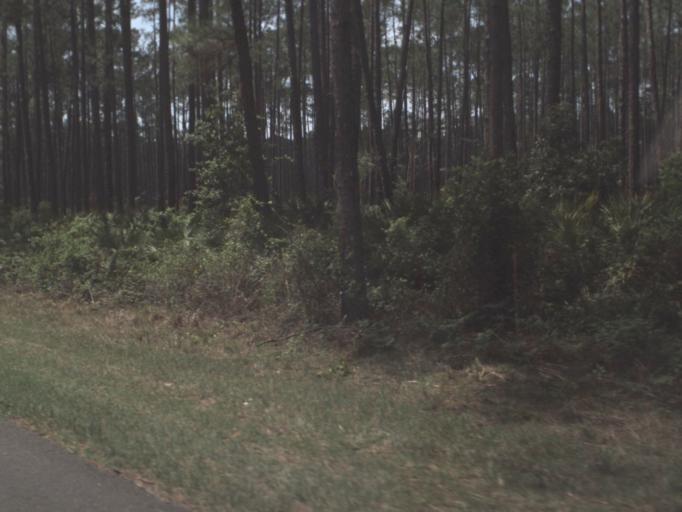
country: US
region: Florida
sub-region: Lake County
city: Umatilla
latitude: 29.0320
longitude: -81.6403
